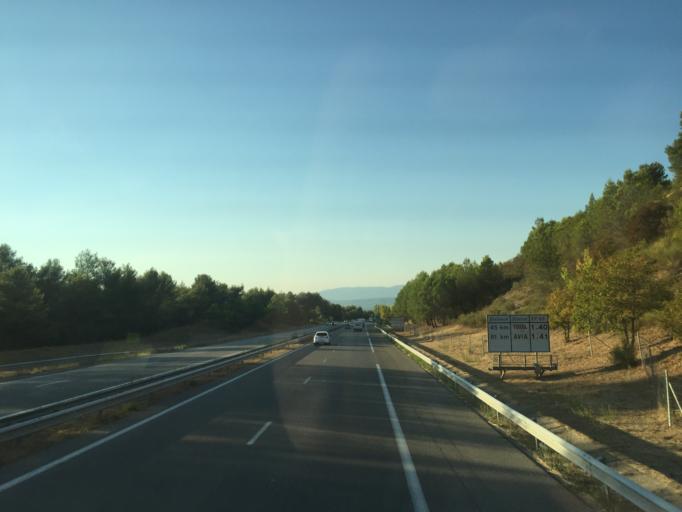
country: FR
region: Provence-Alpes-Cote d'Azur
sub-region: Departement des Bouches-du-Rhone
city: Venelles
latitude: 43.6191
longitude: 5.4945
